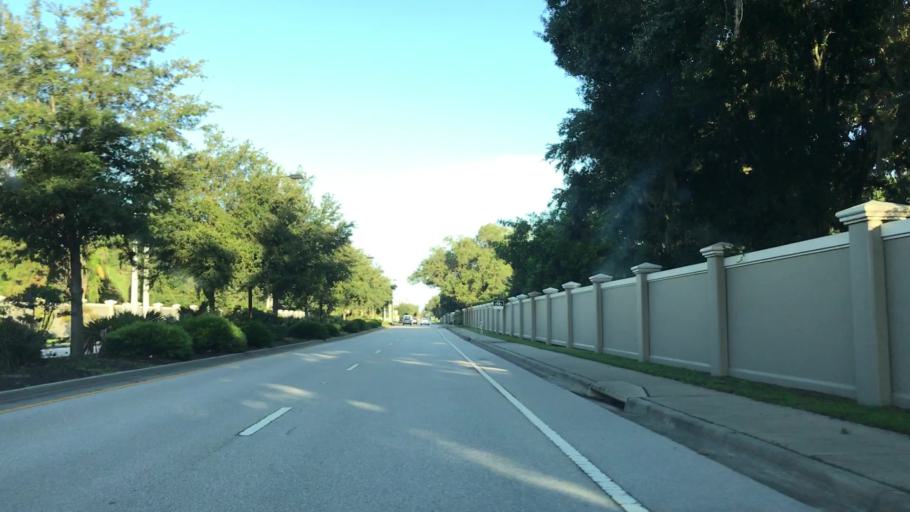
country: US
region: Florida
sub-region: Sarasota County
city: Sarasota Springs
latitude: 27.3231
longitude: -82.4746
